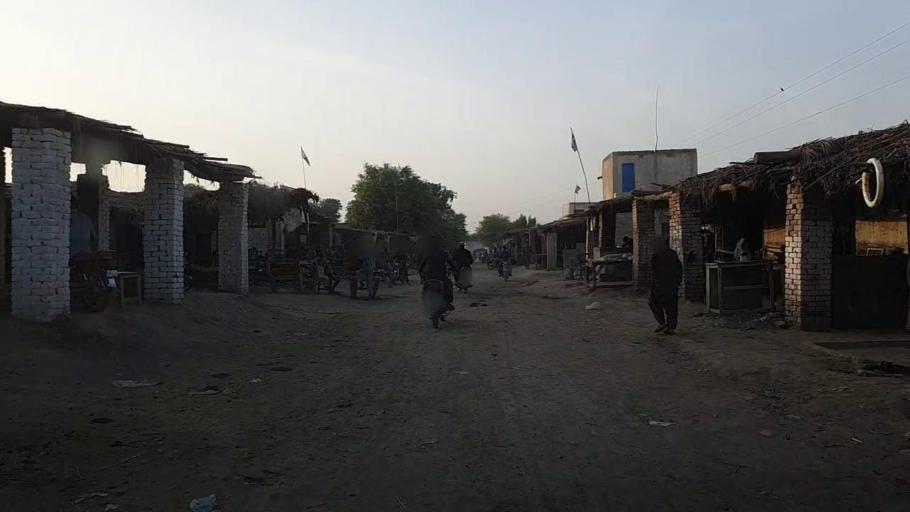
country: PK
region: Sindh
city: Ubauro
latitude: 28.2183
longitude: 69.8214
